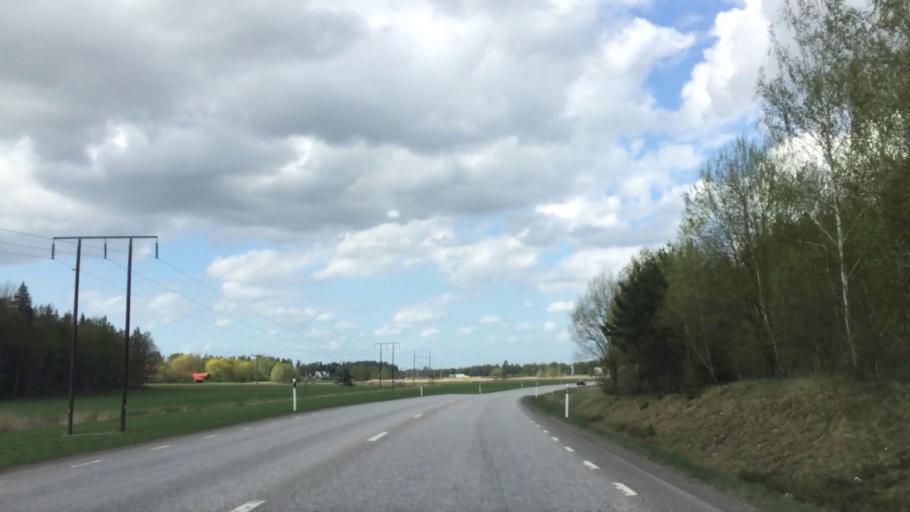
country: SE
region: Soedermanland
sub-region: Eskilstuna Kommun
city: Eskilstuna
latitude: 59.3678
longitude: 16.4627
